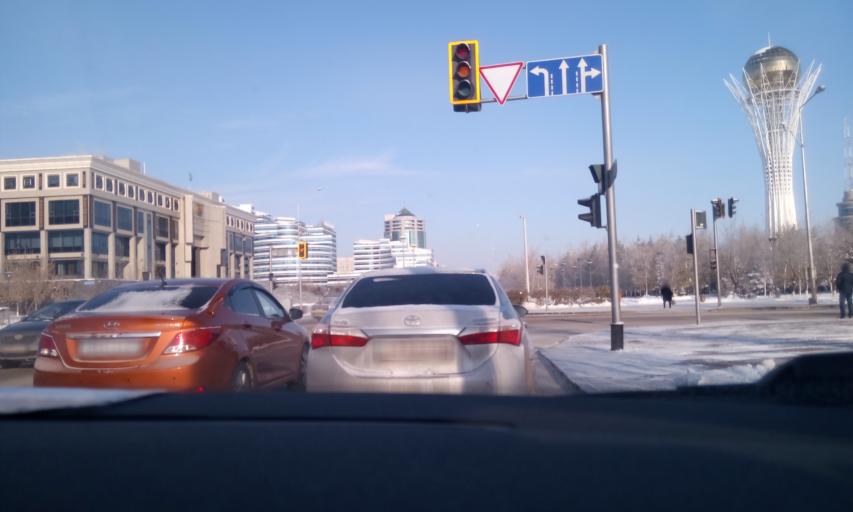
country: KZ
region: Astana Qalasy
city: Astana
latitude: 51.1260
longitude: 71.4277
